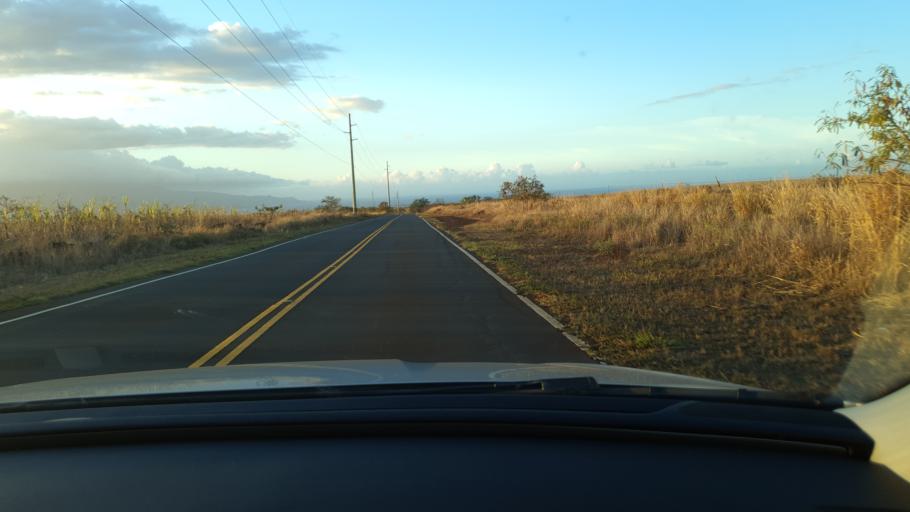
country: US
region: Hawaii
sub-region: Maui County
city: Pukalani
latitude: 20.8099
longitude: -156.3816
